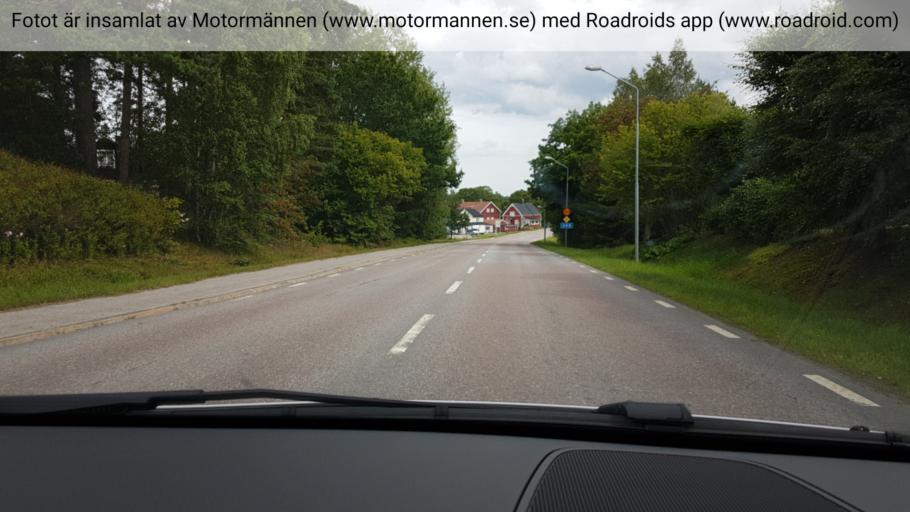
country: SE
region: Uppsala
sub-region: Osthammars Kommun
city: Gimo
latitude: 60.2160
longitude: 18.1988
